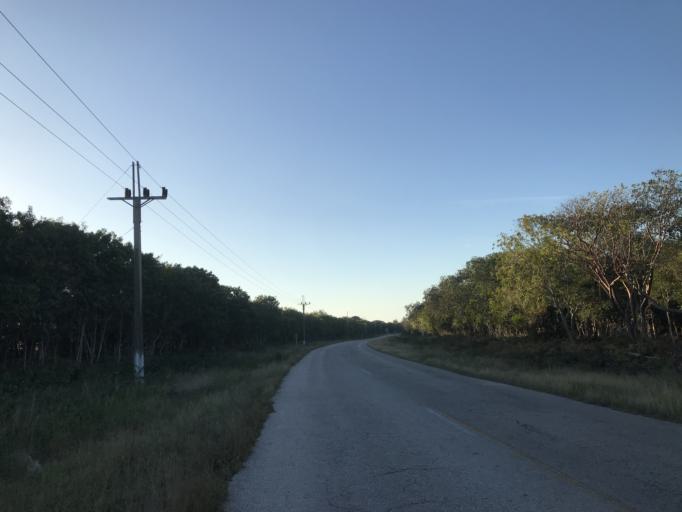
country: CU
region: Cienfuegos
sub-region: Municipio de Aguada de Pasajeros
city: Aguada de Pasajeros
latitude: 22.0677
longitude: -81.0478
